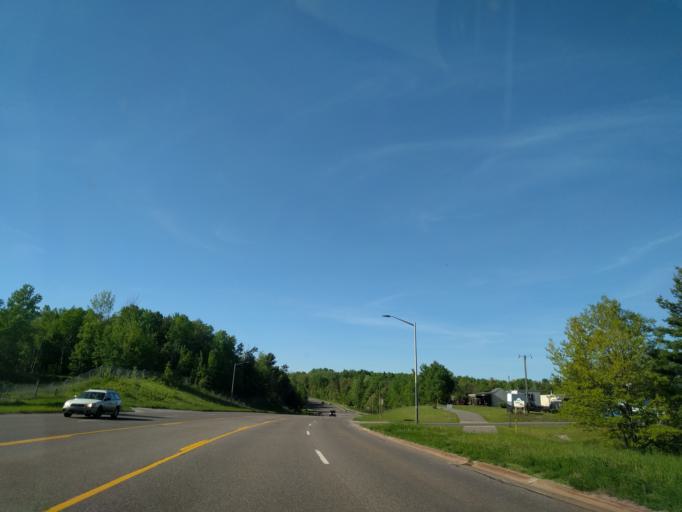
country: US
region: Michigan
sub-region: Marquette County
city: Marquette
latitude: 46.5243
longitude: -87.4170
